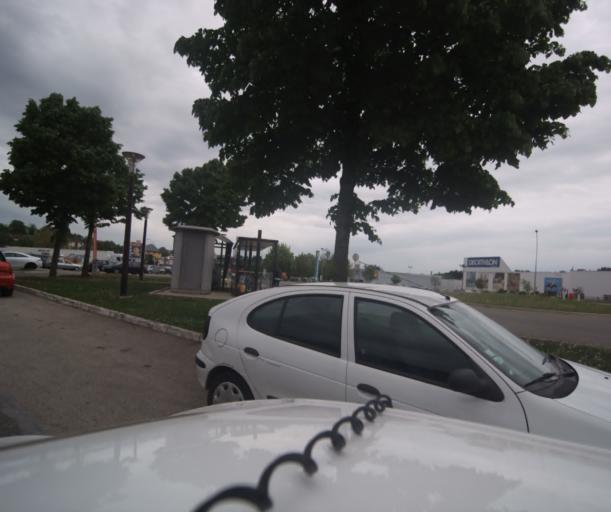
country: FR
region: Franche-Comte
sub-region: Departement du Doubs
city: Avanne-Aveney
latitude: 47.2157
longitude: 5.9490
